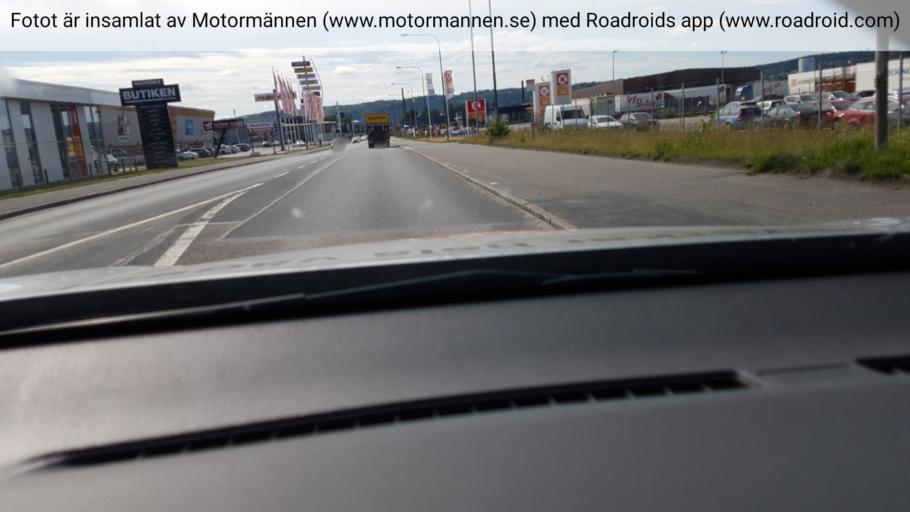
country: SE
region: Joenkoeping
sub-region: Jonkopings Kommun
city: Jonkoping
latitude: 57.7619
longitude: 14.1798
